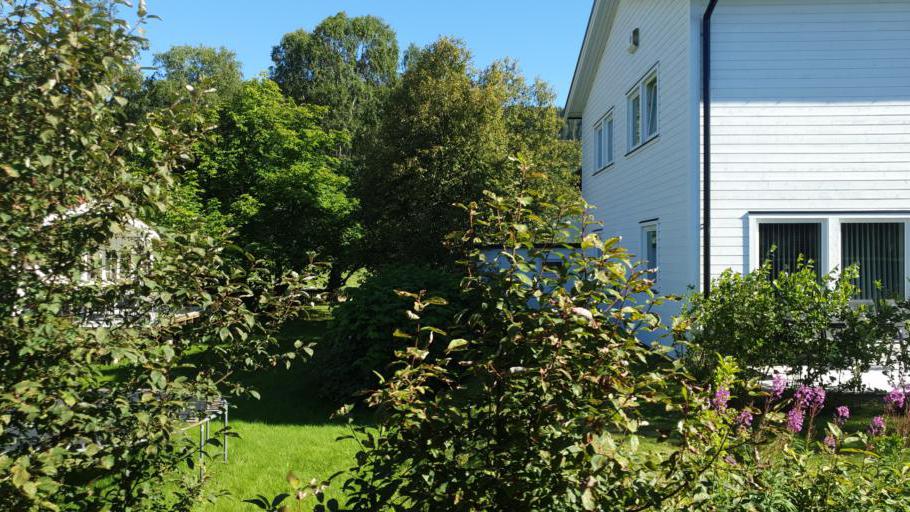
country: NO
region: Sor-Trondelag
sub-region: Orkdal
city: Orkanger
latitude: 63.2813
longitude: 9.8329
